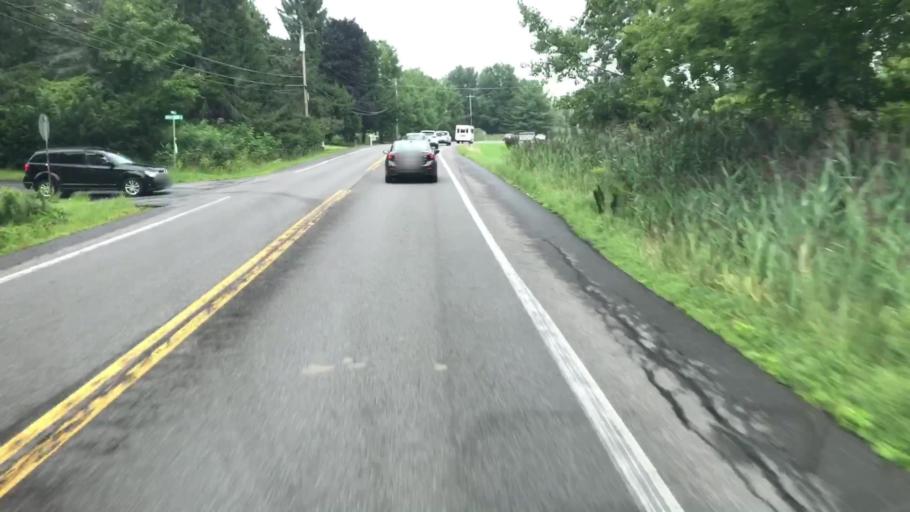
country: US
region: New York
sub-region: Onondaga County
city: Liverpool
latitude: 43.1801
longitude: -76.2150
